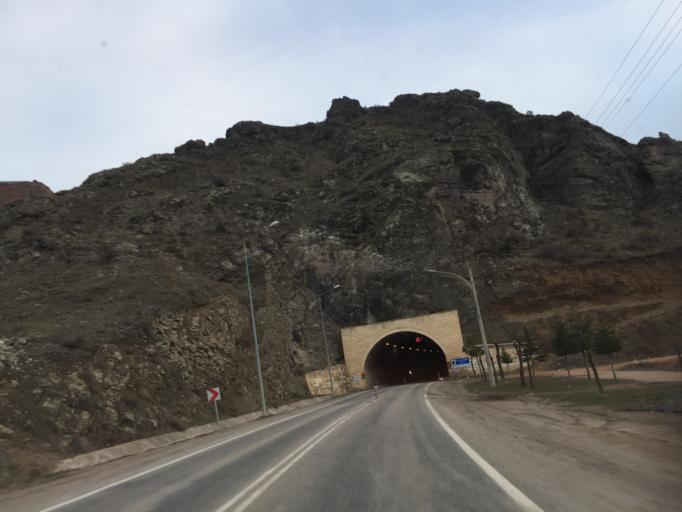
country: TR
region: Gumushane
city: Gumushkhane
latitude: 40.4738
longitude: 39.4641
